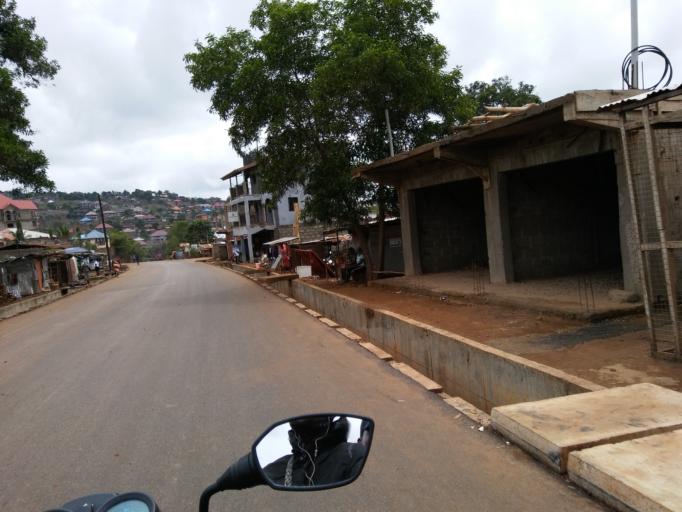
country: SL
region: Western Area
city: Hastings
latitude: 8.3962
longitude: -13.1549
